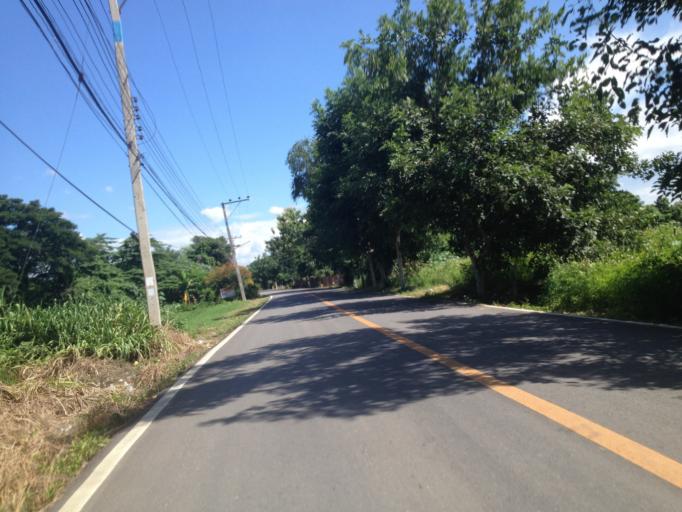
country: TH
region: Chiang Mai
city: Hang Dong
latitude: 18.6792
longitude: 98.9799
